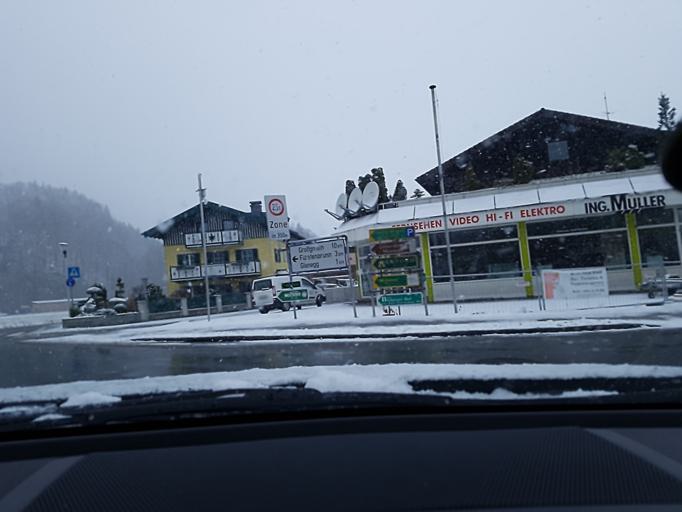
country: AT
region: Salzburg
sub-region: Politischer Bezirk Salzburg-Umgebung
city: Grodig
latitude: 47.7423
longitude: 13.0337
